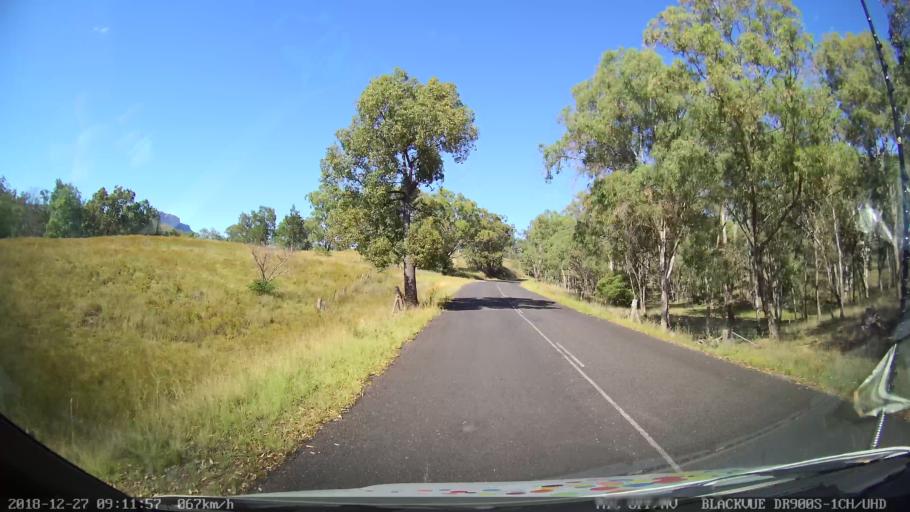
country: AU
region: New South Wales
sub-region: Lithgow
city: Portland
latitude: -33.1383
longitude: 150.1098
